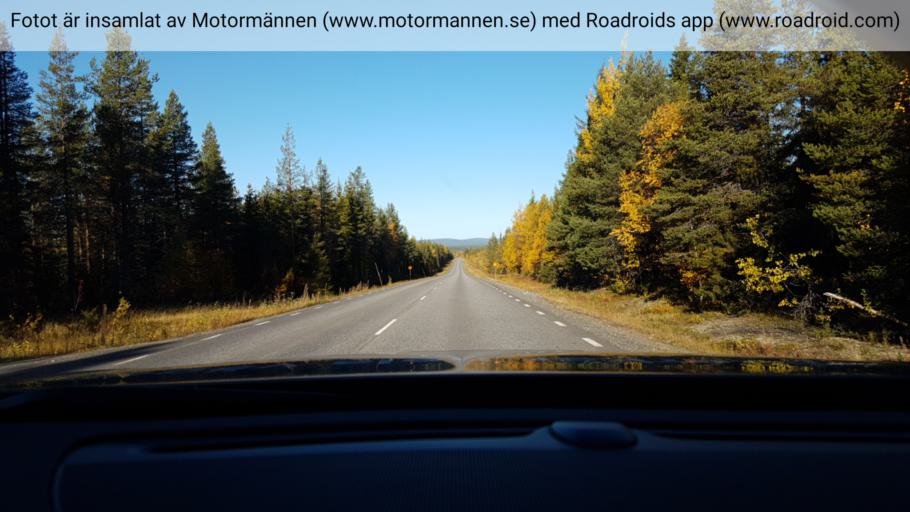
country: SE
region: Vaesterbotten
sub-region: Skelleftea Kommun
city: Storvik
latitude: 65.3622
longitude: 20.4257
